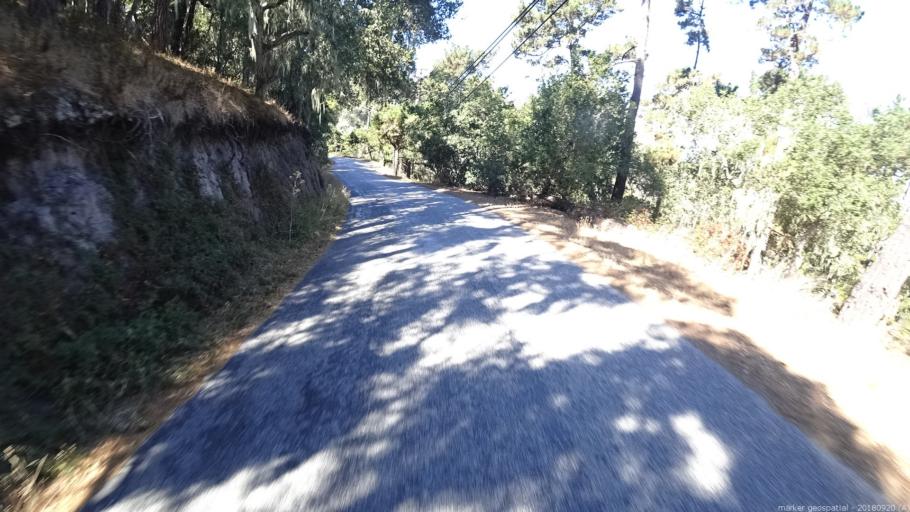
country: US
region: California
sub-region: Monterey County
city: Monterey
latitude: 36.5741
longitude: -121.8919
